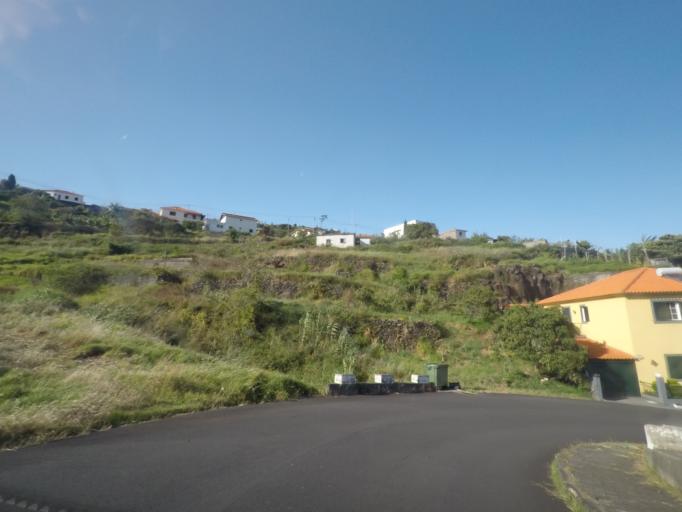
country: PT
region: Madeira
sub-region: Santa Cruz
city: Santa Cruz
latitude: 32.6911
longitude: -16.7931
